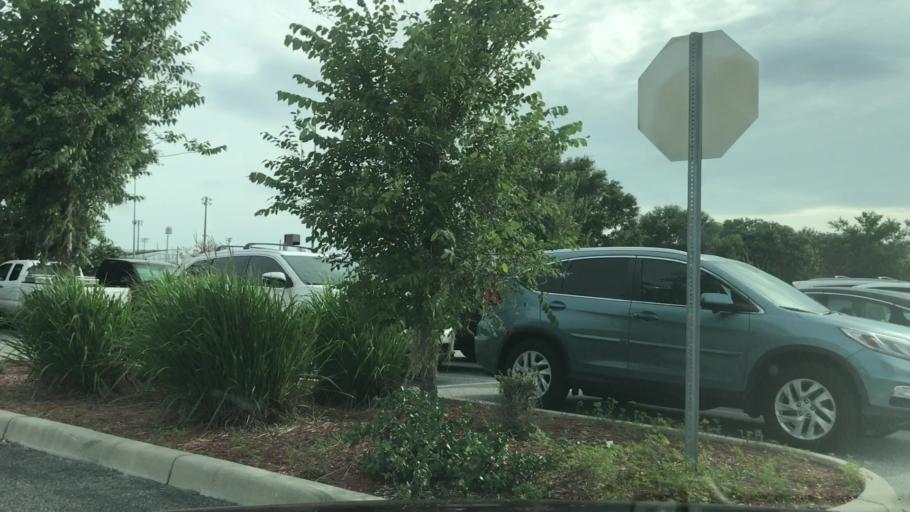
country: US
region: Florida
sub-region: Sarasota County
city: The Meadows
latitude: 27.4491
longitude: -82.4345
